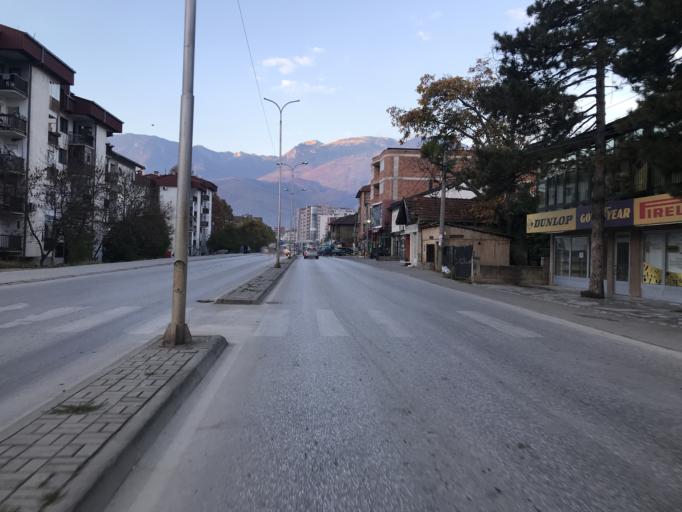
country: XK
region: Pec
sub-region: Komuna e Pejes
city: Peje
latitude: 42.6695
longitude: 20.3073
